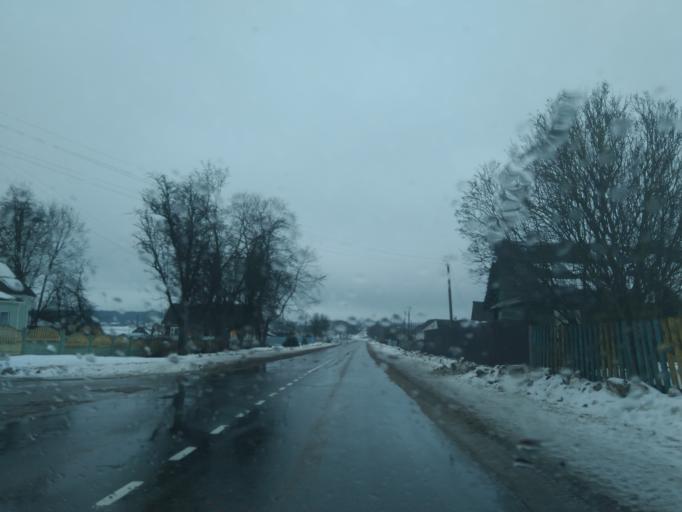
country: BY
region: Minsk
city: Stowbtsy
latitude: 53.5813
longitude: 26.8318
